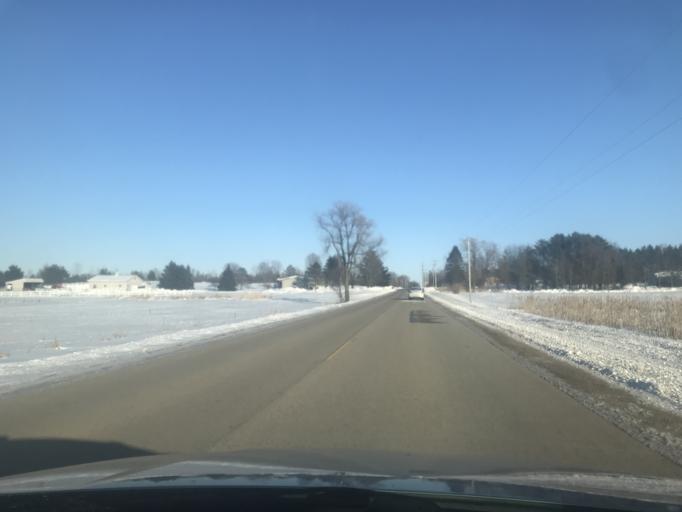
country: US
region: Wisconsin
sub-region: Marinette County
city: Marinette
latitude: 45.1450
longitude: -87.6597
